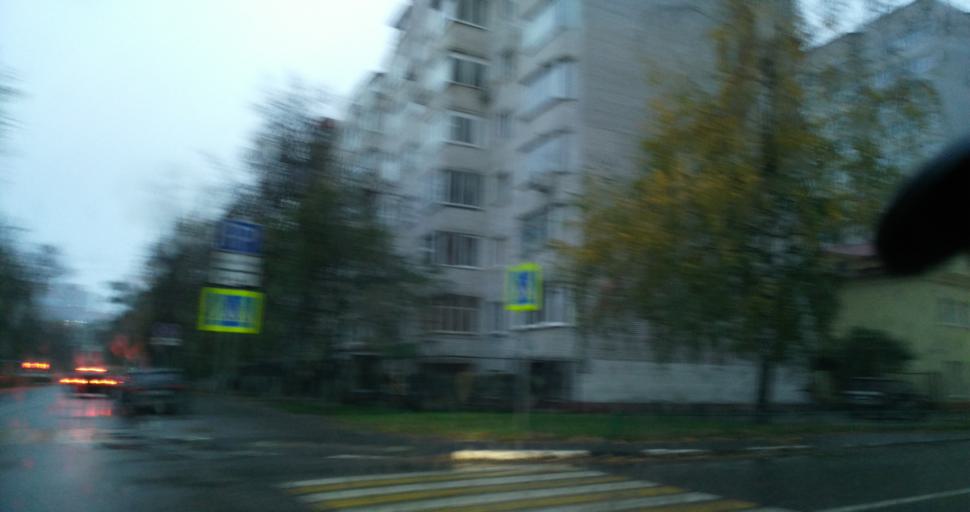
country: RU
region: Moscow
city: Khimki
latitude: 55.8937
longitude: 37.4388
